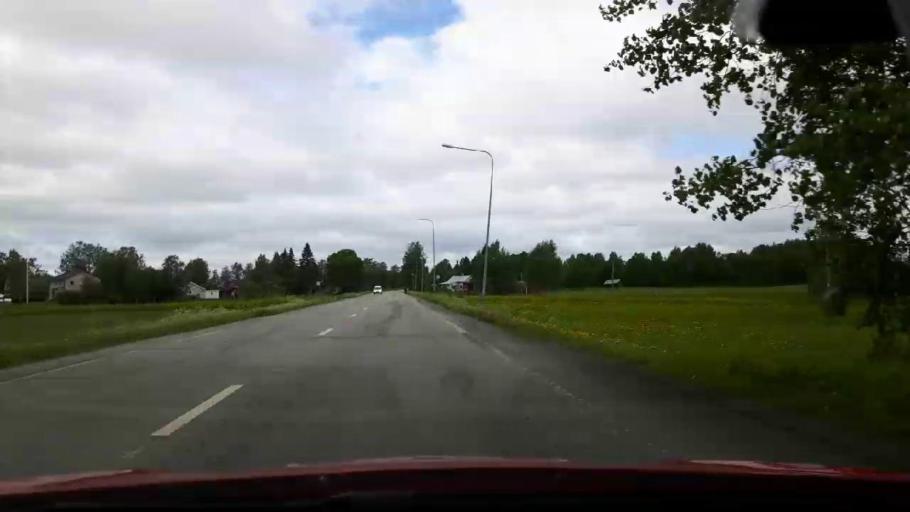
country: SE
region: Jaemtland
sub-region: Krokoms Kommun
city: Krokom
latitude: 63.3081
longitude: 14.4645
